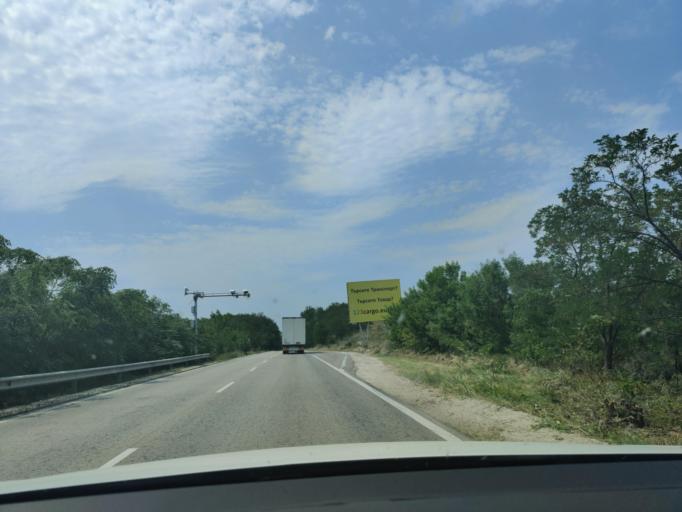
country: BG
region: Vidin
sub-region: Obshtina Vidin
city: Dunavtsi
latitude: 43.8788
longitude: 22.7896
